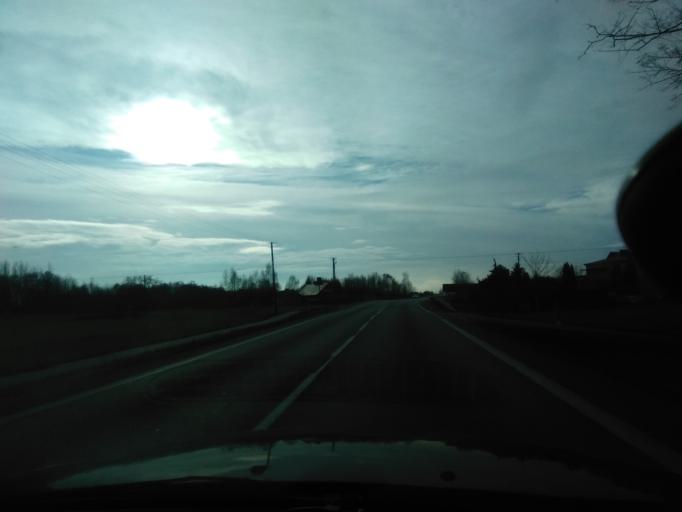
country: PL
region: Subcarpathian Voivodeship
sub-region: Powiat krosnienski
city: Kroscienko Wyzne
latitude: 49.6719
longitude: 21.8476
